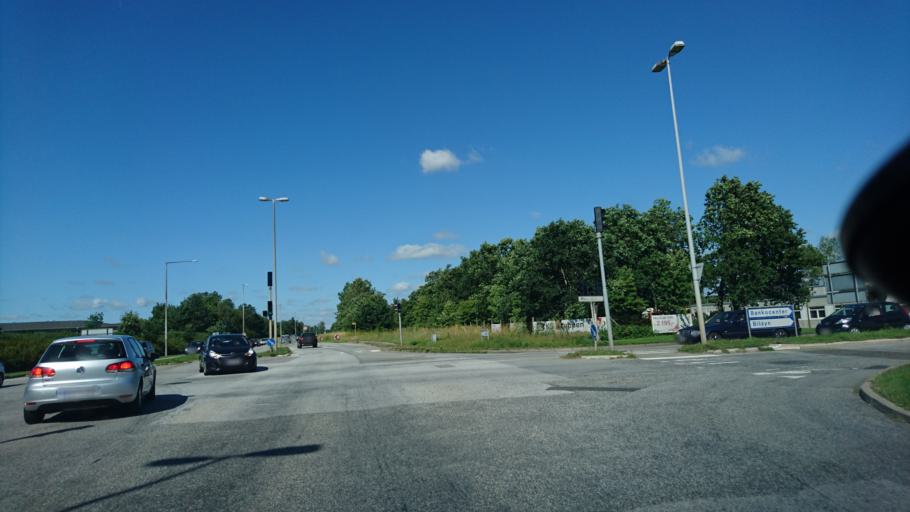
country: DK
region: North Denmark
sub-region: Alborg Kommune
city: Gistrup
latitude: 57.0243
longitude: 10.0070
